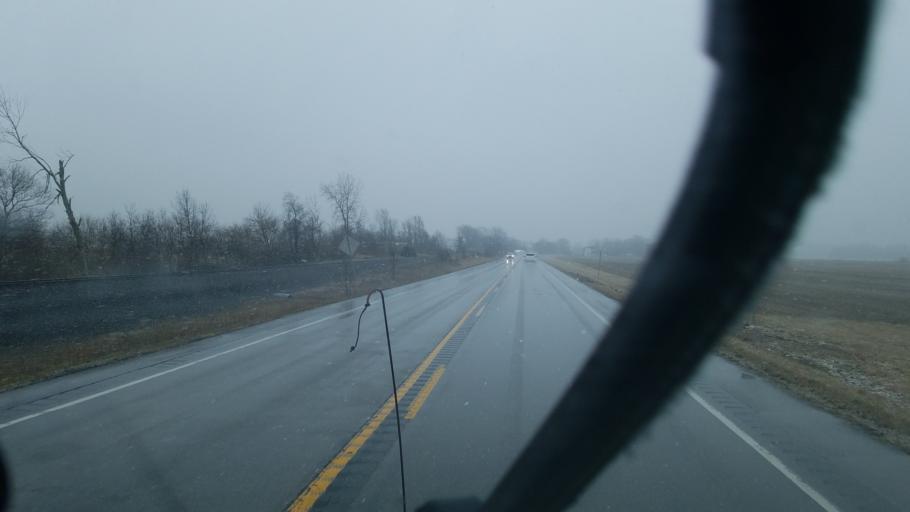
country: US
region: Indiana
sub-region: Wabash County
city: Mount Vernon
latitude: 40.6663
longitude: -85.7194
